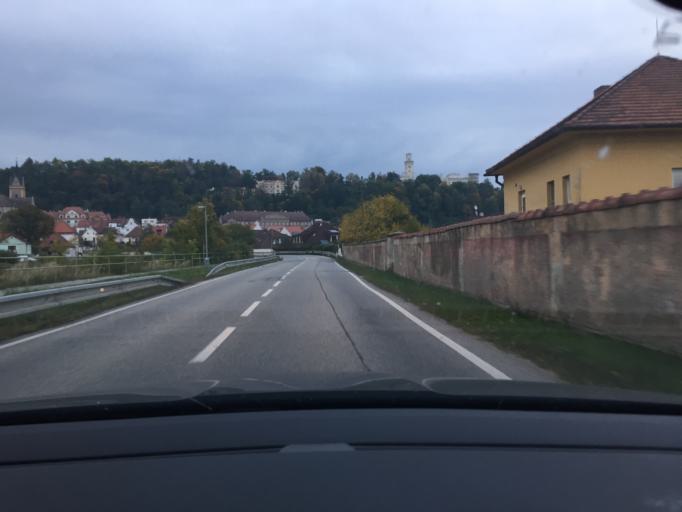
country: CZ
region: Jihocesky
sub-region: Okres Ceske Budejovice
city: Hluboka nad Vltavou
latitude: 49.0474
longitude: 14.4332
